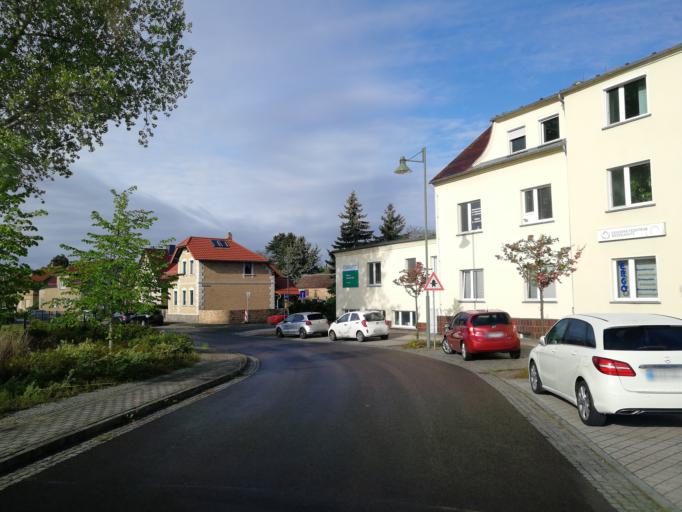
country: DE
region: Brandenburg
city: Lauchhammer
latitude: 51.4958
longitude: 13.7526
